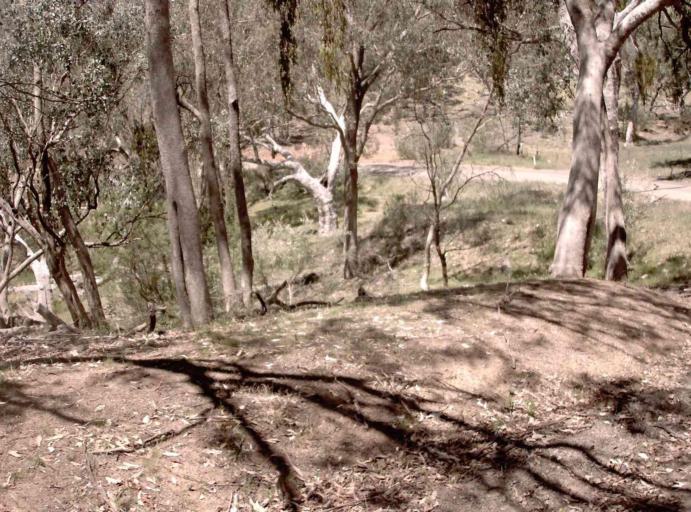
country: AU
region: New South Wales
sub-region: Snowy River
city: Jindabyne
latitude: -37.0871
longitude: 148.4460
